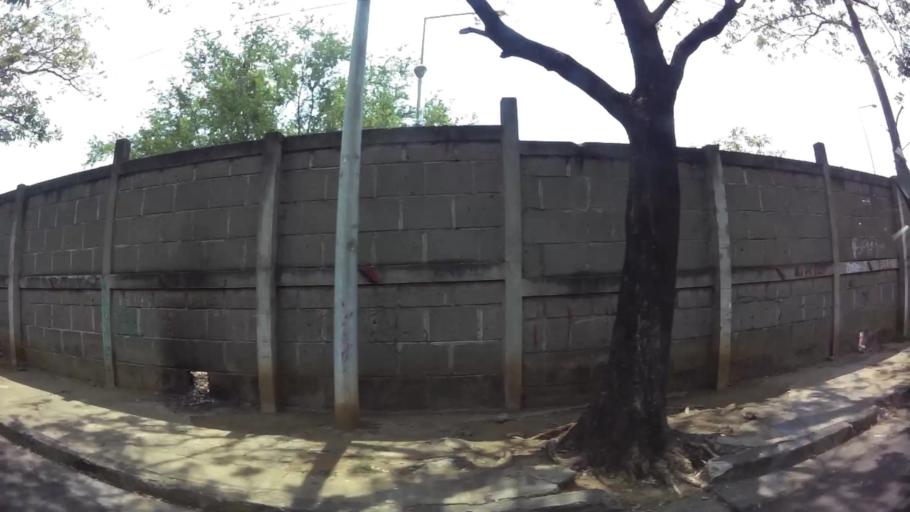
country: NI
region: Managua
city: Managua
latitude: 12.1544
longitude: -86.2934
